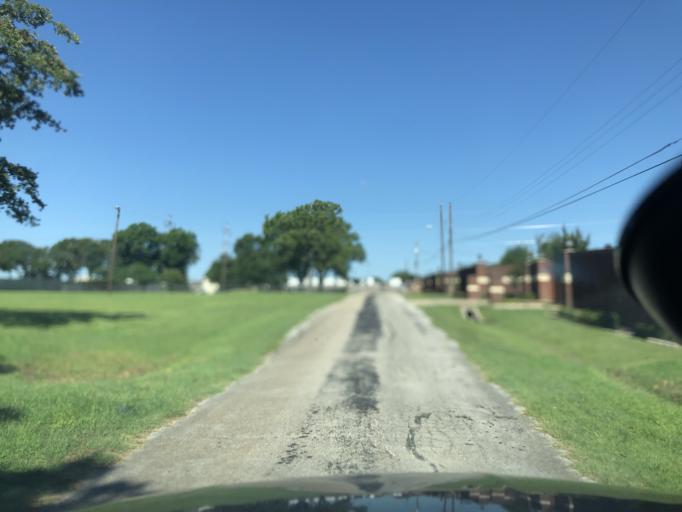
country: US
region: Texas
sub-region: Tarrant County
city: Euless
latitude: 32.8080
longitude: -97.0230
